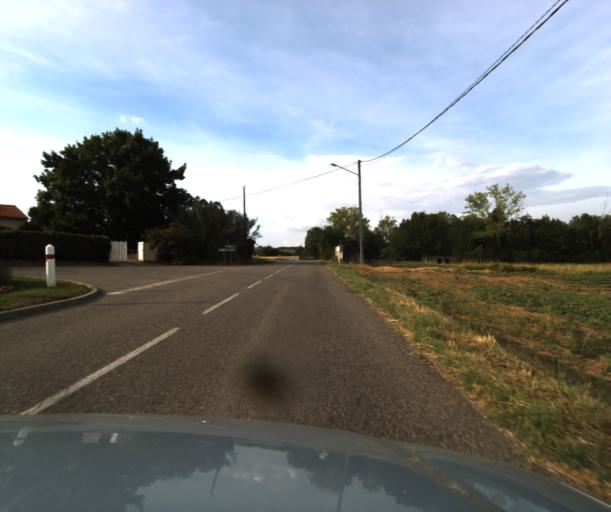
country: FR
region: Midi-Pyrenees
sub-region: Departement du Tarn-et-Garonne
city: Castelsarrasin
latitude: 43.9511
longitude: 1.1025
